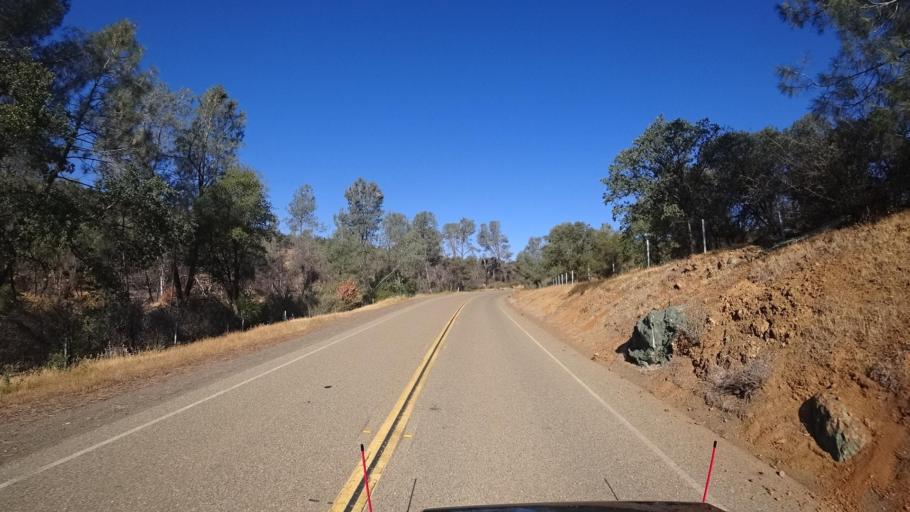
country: US
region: California
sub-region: Mariposa County
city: Mariposa
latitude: 37.5678
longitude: -120.1376
